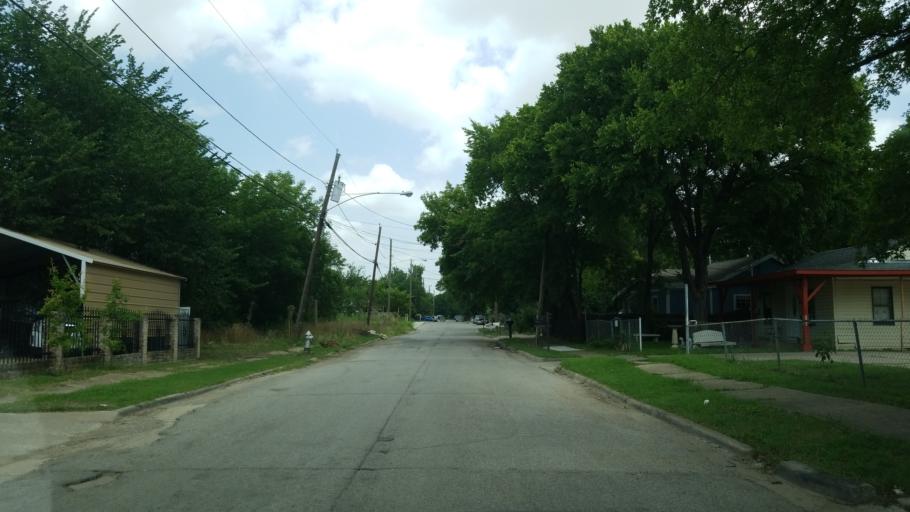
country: US
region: Texas
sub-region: Dallas County
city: Irving
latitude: 32.7908
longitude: -96.9025
